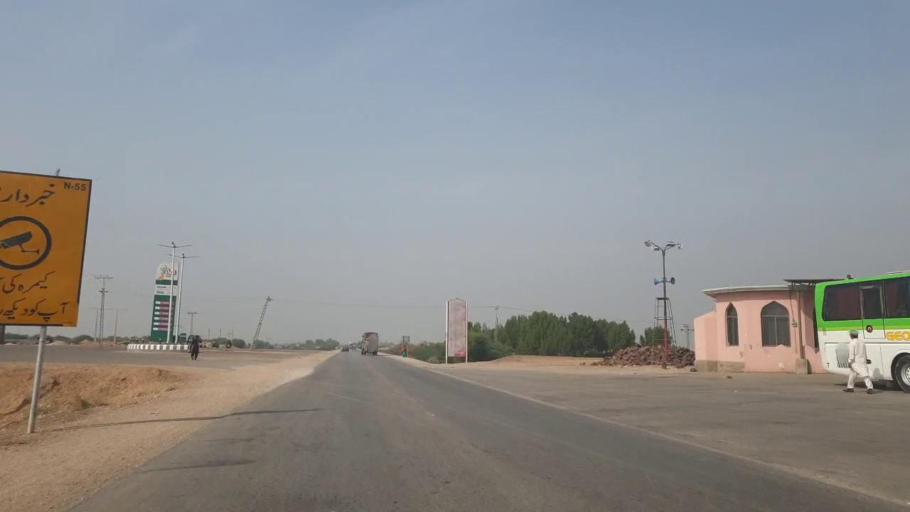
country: PK
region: Sindh
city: Sann
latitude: 26.1601
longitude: 68.0212
